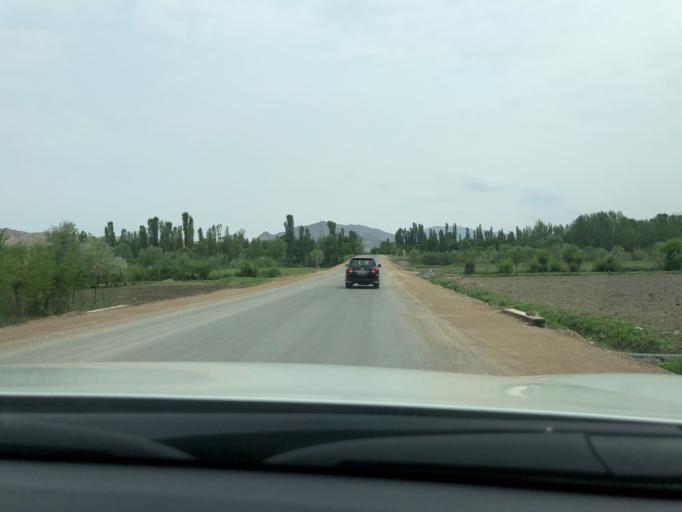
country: TJ
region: Viloyati Sughd
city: Isfara
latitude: 40.1485
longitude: 70.6138
